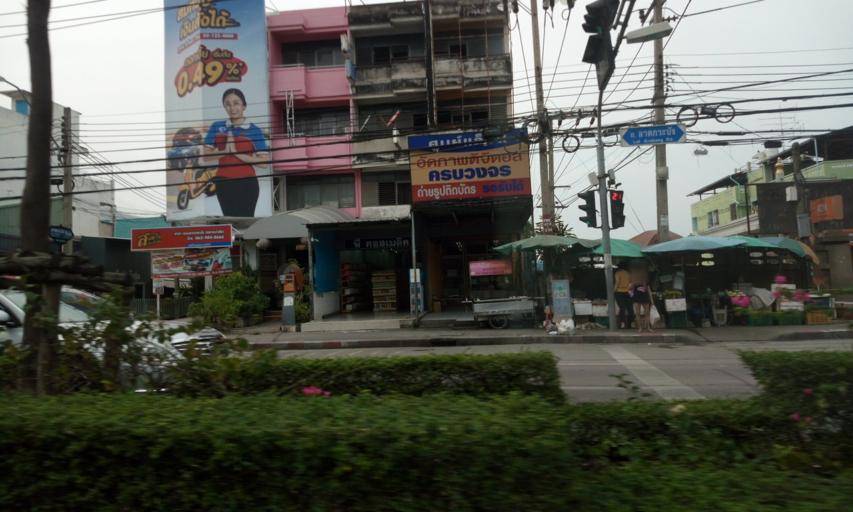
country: TH
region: Bangkok
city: Saphan Sung
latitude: 13.7221
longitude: 100.7115
